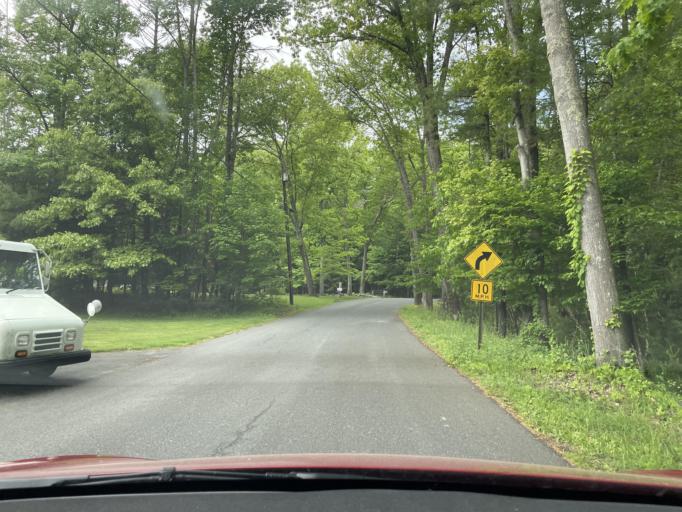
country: US
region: New York
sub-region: Ulster County
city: West Hurley
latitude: 42.0152
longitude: -74.0997
